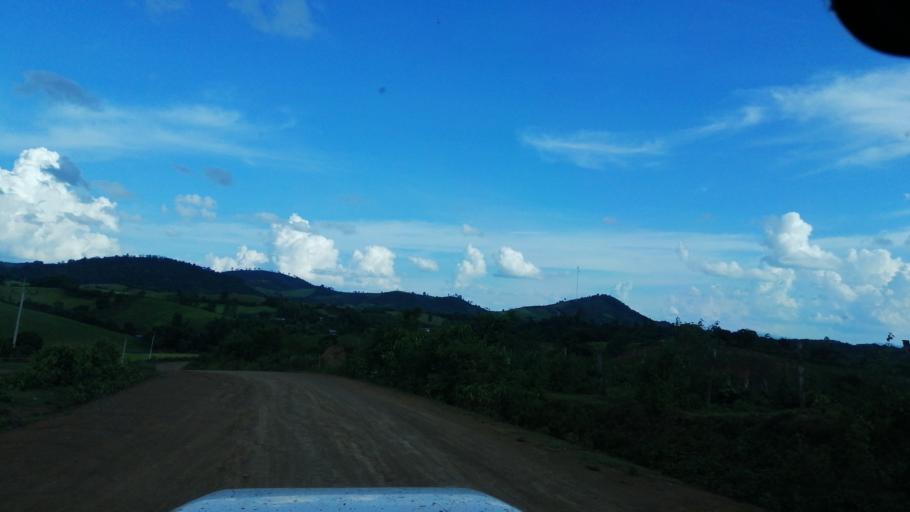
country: LA
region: Xiagnabouli
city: Muang Kenthao
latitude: 17.8521
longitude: 101.2408
